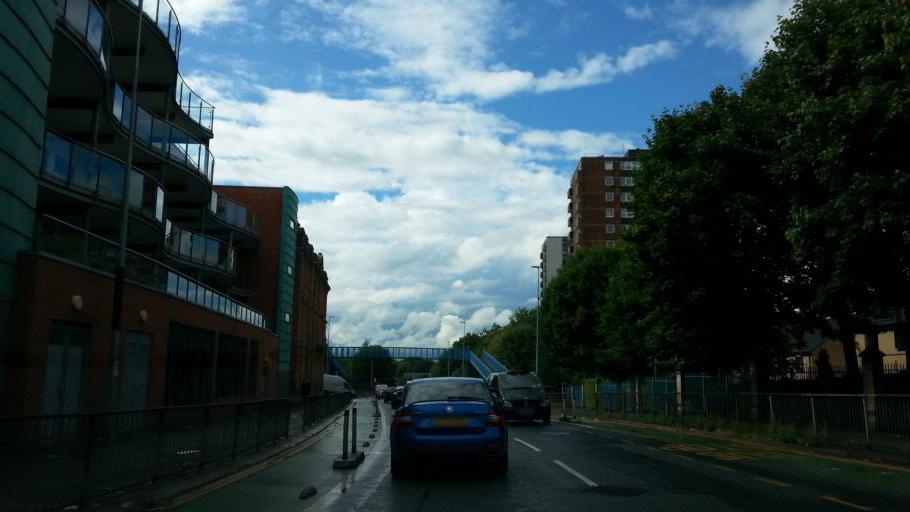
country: GB
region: England
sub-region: Manchester
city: Manchester
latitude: 53.4882
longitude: -2.2560
